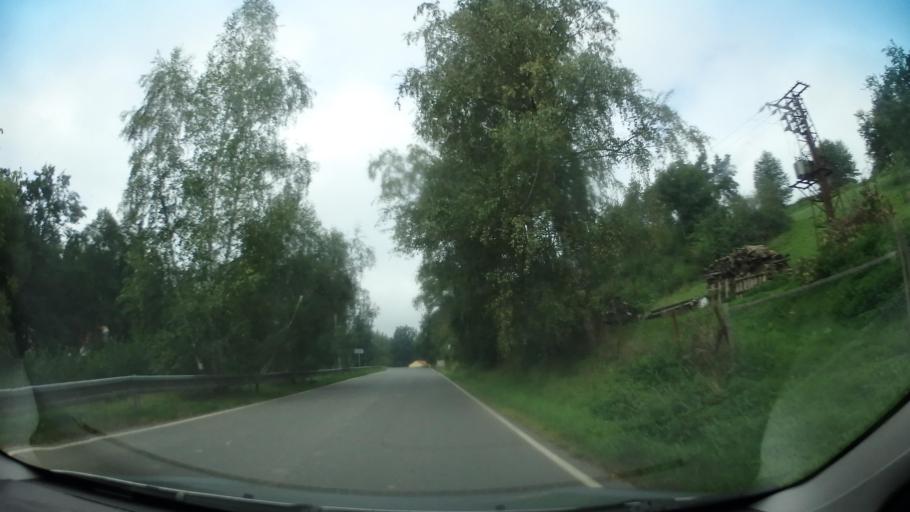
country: CZ
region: Central Bohemia
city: Kosova Hora
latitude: 49.7213
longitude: 14.4711
